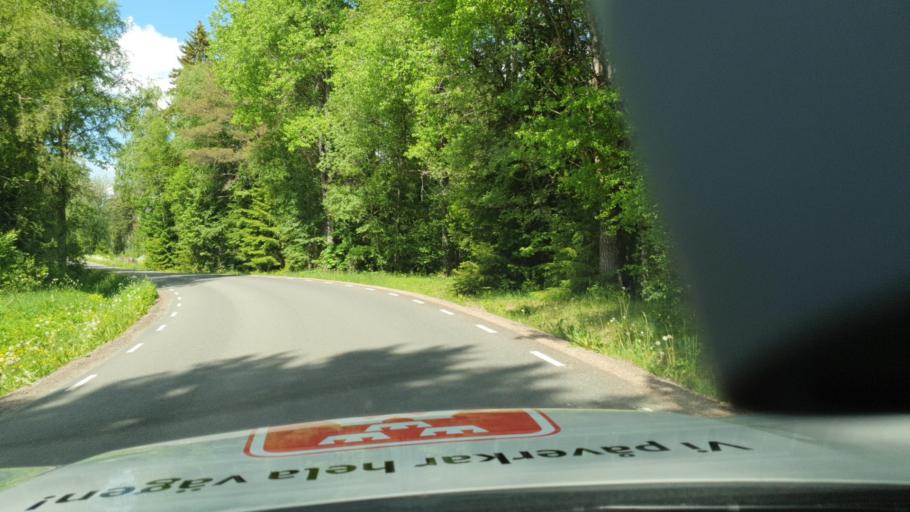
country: SE
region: Joenkoeping
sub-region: Mullsjo Kommun
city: Mullsjoe
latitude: 58.0071
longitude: 13.7183
